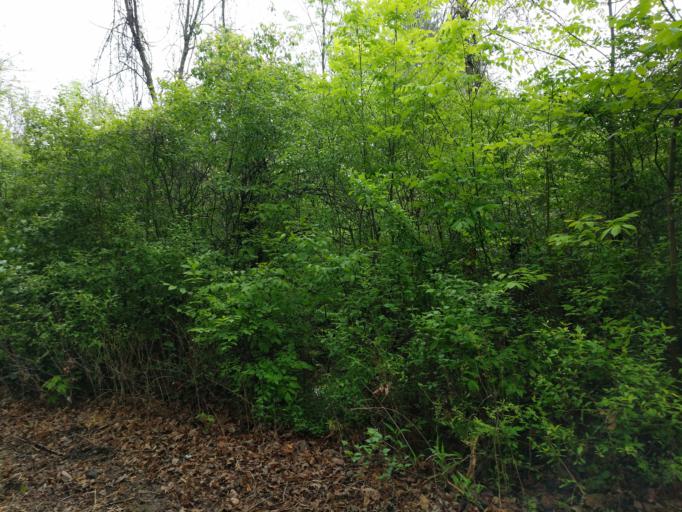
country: US
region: Michigan
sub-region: Eaton County
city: Waverly
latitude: 42.7660
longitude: -84.6367
